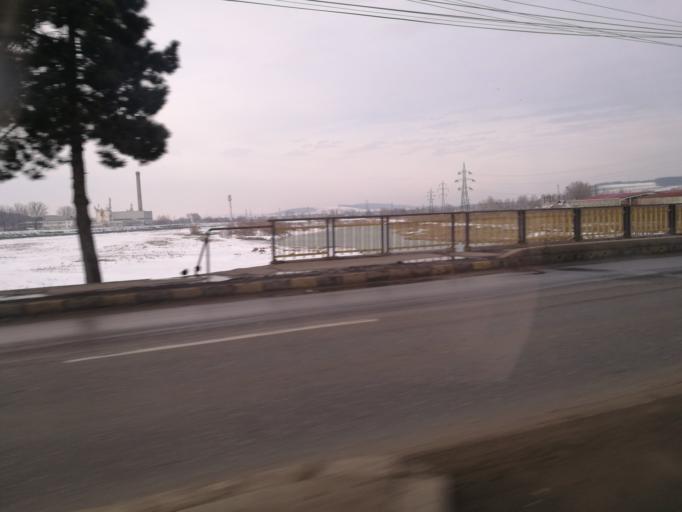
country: RO
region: Suceava
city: Suceava
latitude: 47.6581
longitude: 26.2635
